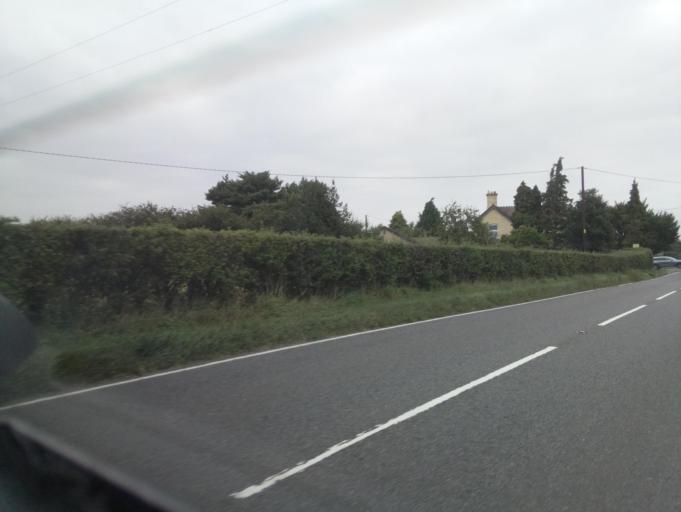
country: GB
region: England
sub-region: Shropshire
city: Astley
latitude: 52.7574
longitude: -2.6954
